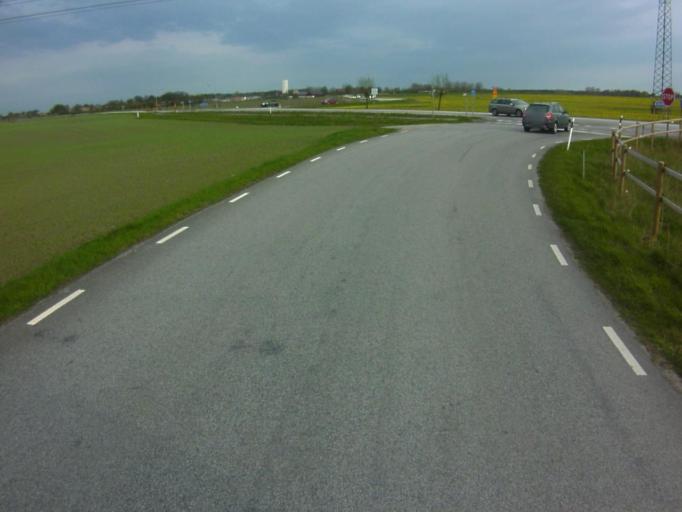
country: SE
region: Skane
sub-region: Kavlinge Kommun
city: Hofterup
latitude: 55.7655
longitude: 12.9751
